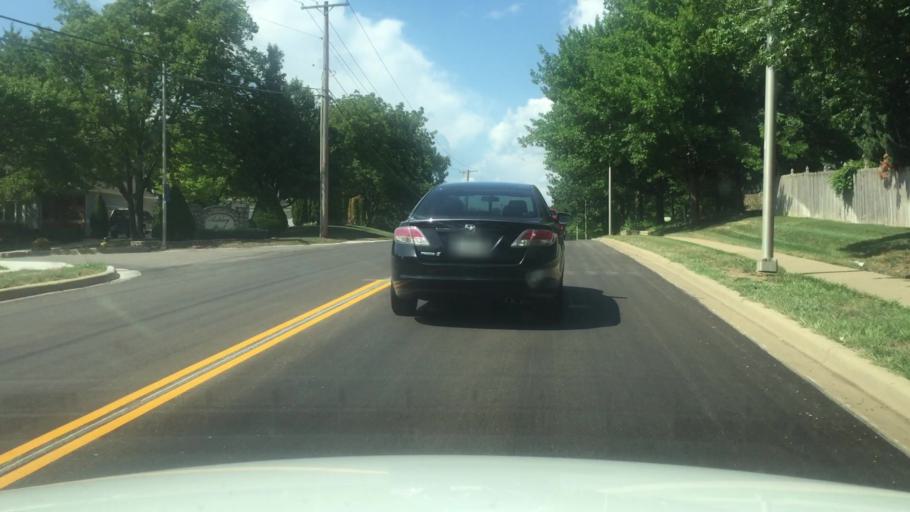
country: US
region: Kansas
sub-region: Johnson County
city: Lenexa
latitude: 38.9899
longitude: -94.7423
